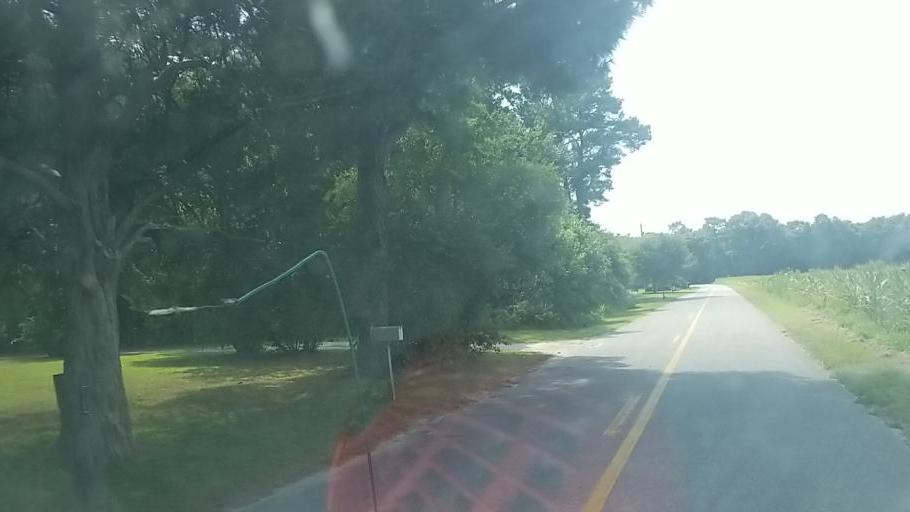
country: US
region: Maryland
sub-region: Worcester County
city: Snow Hill
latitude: 38.2521
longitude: -75.3866
